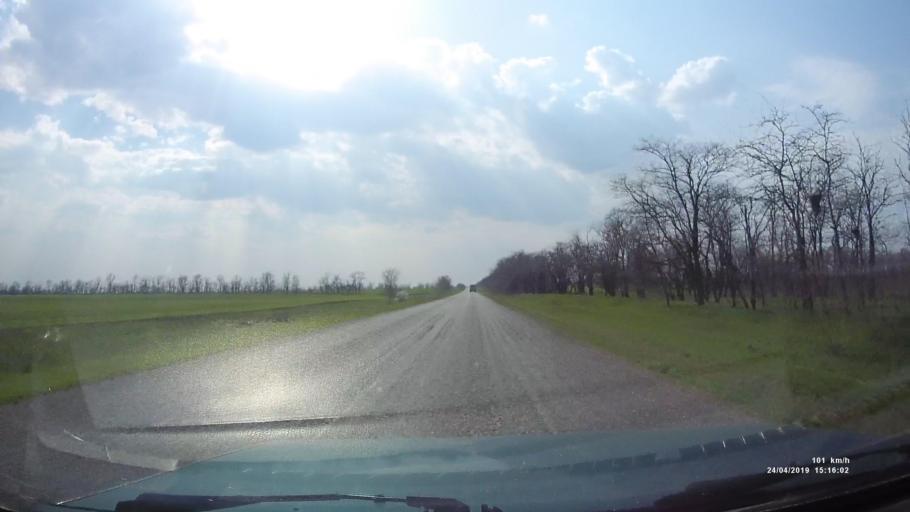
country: RU
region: Rostov
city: Remontnoye
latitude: 46.5471
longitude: 43.2224
